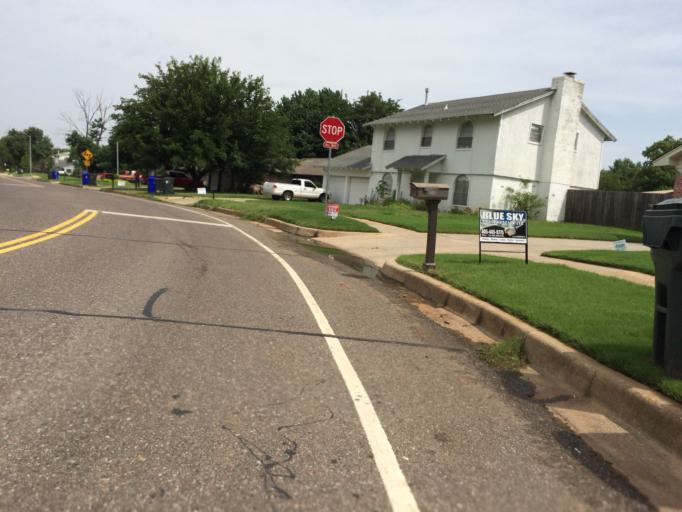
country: US
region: Oklahoma
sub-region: Cleveland County
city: Norman
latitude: 35.1998
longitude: -97.4109
